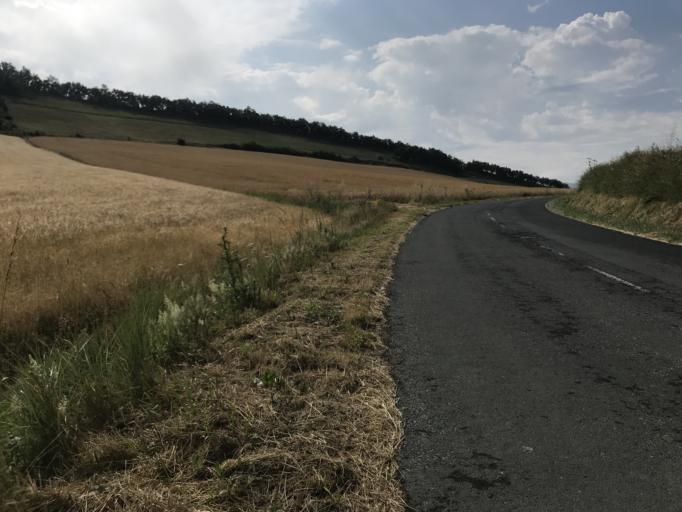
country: ES
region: Basque Country
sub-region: Provincia de Alava
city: Gasteiz / Vitoria
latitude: 42.8227
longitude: -2.6480
